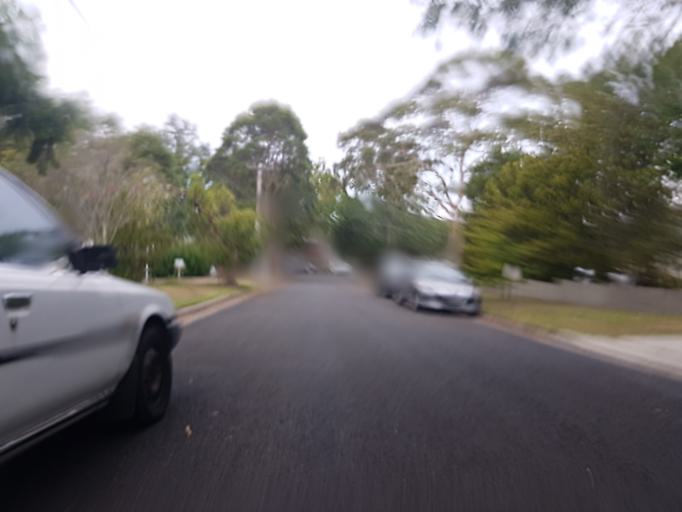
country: AU
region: New South Wales
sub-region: Warringah
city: Forestville
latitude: -33.7584
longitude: 151.2119
